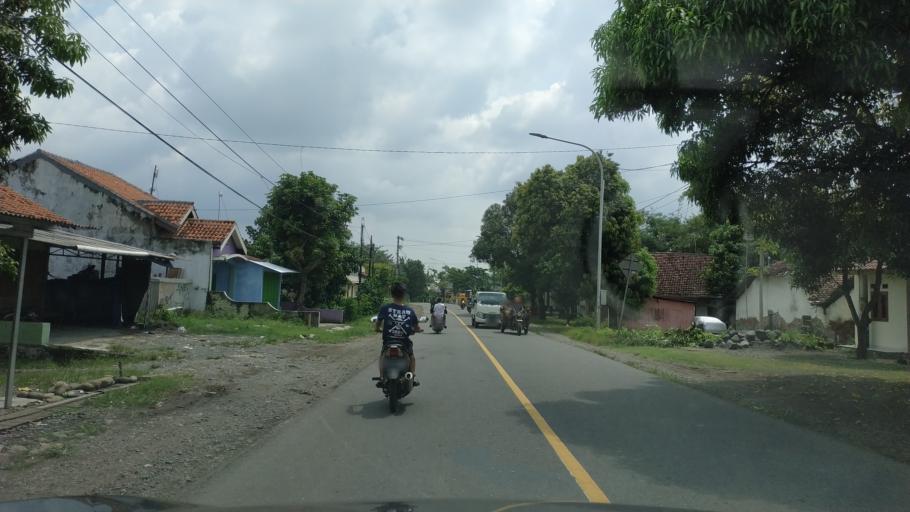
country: ID
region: Central Java
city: Lebaksiu
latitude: -7.0348
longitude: 109.1457
